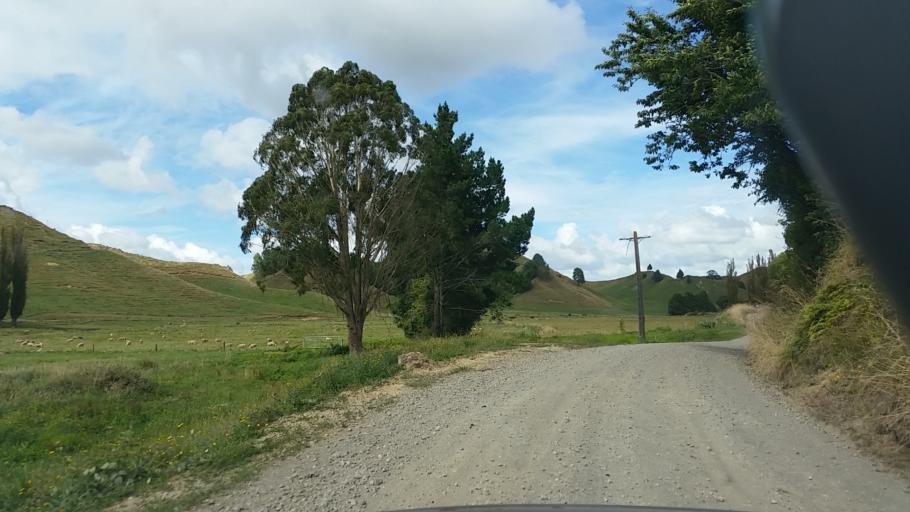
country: NZ
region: Taranaki
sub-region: South Taranaki District
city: Eltham
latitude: -39.2526
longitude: 174.5330
